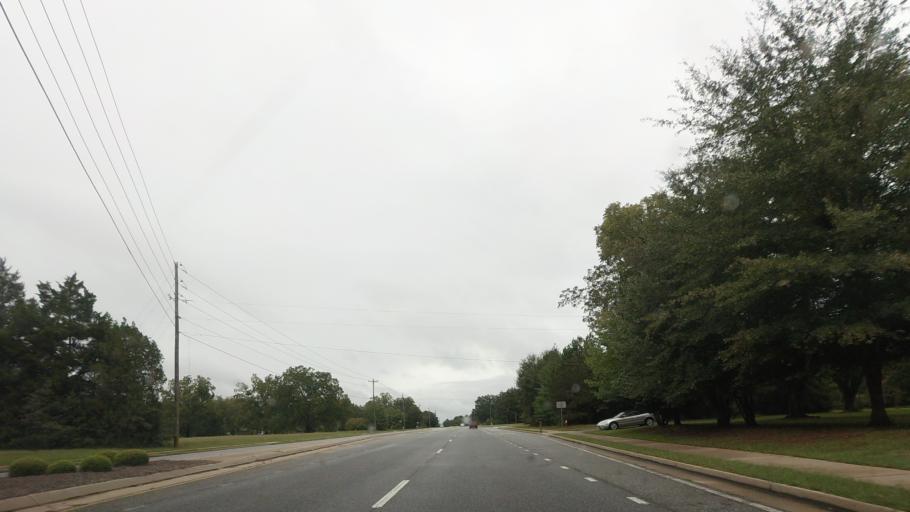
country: US
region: Georgia
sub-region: Houston County
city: Centerville
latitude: 32.5427
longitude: -83.6596
